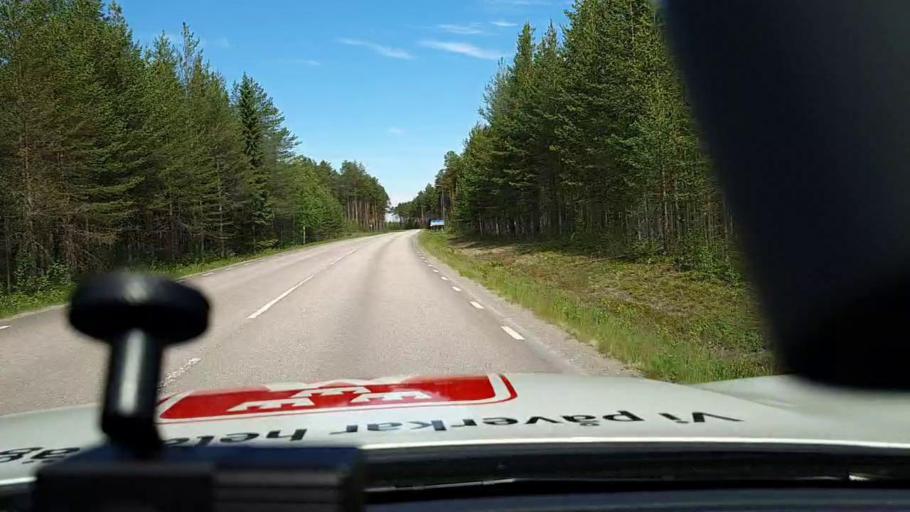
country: SE
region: Norrbotten
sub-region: Lulea Kommun
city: Sodra Sunderbyn
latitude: 65.6292
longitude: 21.9265
